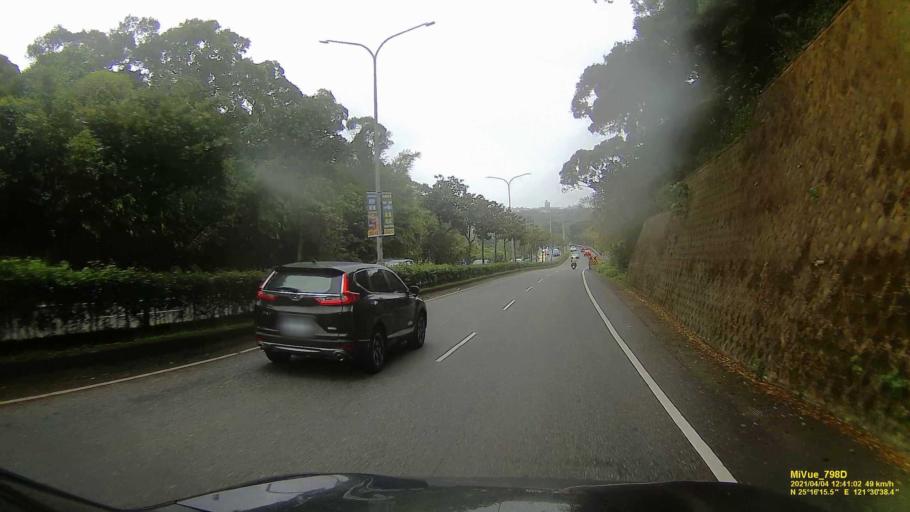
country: TW
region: Taipei
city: Taipei
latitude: 25.2708
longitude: 121.5105
